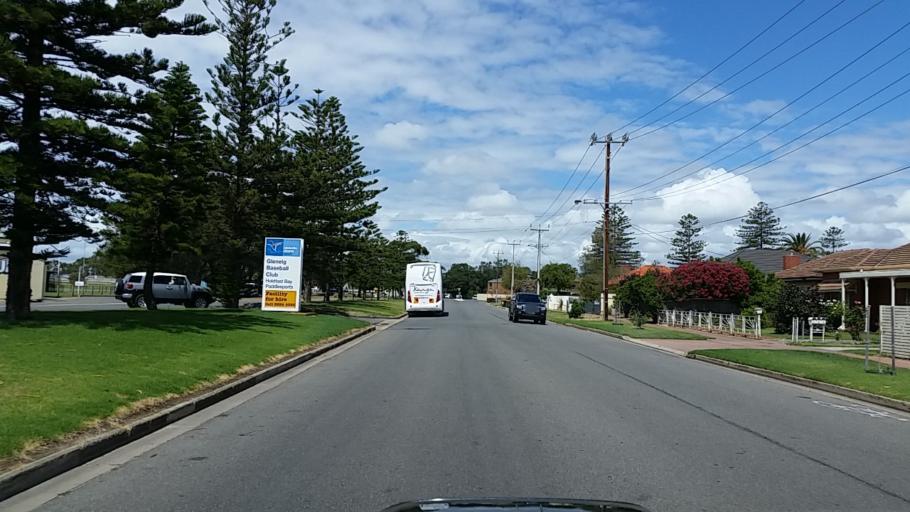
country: AU
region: South Australia
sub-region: Adelaide
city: Glenelg
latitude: -34.9640
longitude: 138.5144
